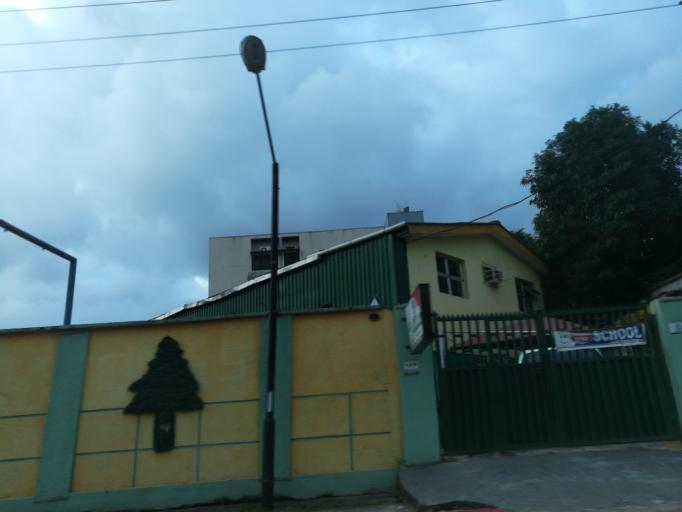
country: NG
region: Lagos
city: Ikeja
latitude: 6.6078
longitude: 3.3420
